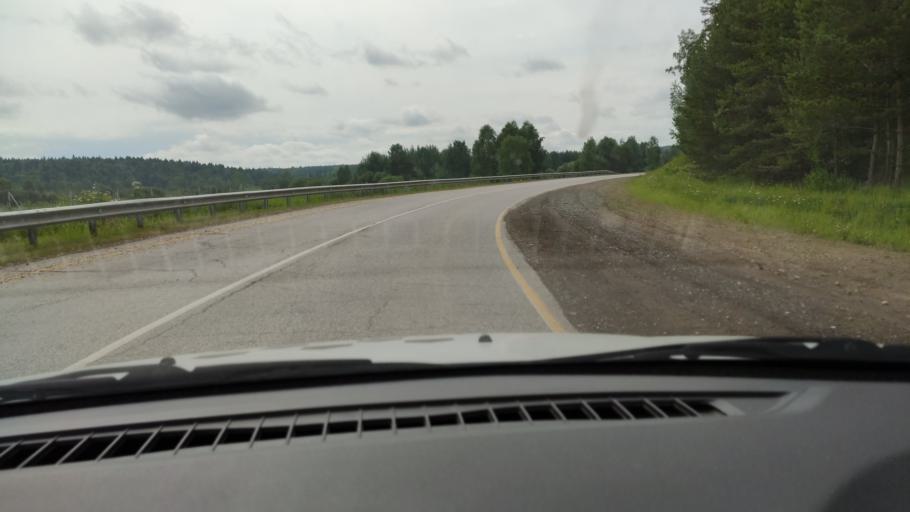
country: RU
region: Perm
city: Kukushtan
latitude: 57.4886
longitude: 56.6288
